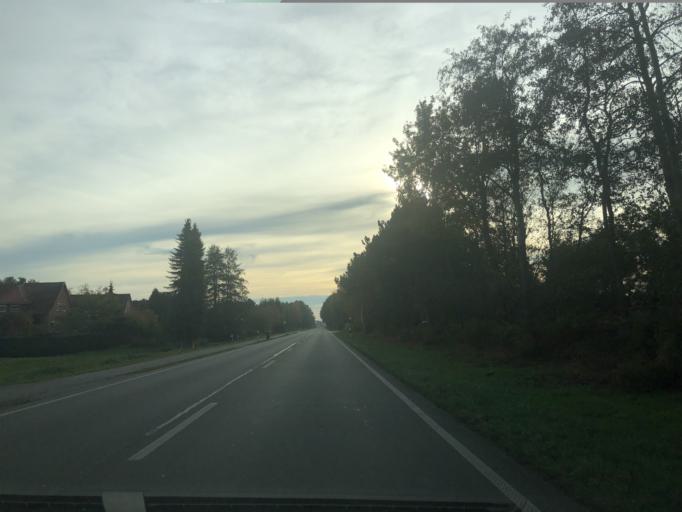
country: DE
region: Lower Saxony
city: Edewecht
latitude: 53.0785
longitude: 7.9318
